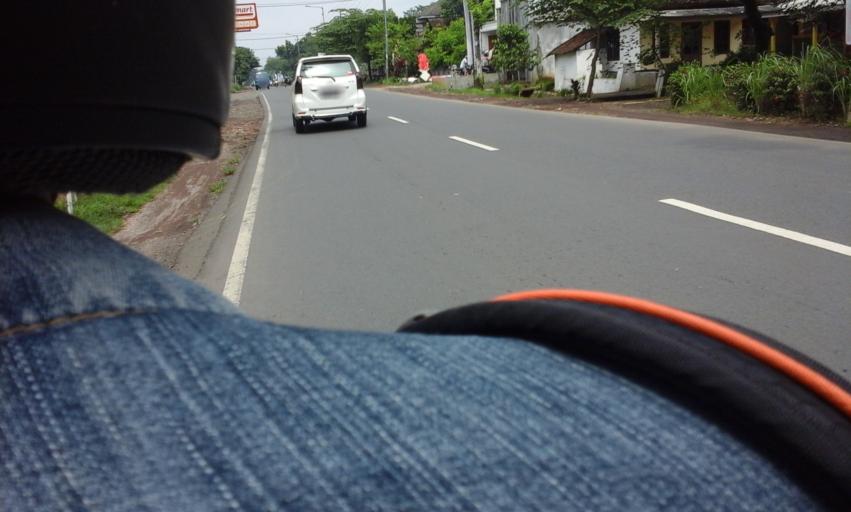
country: ID
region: East Java
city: Klatakan
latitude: -8.1898
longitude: 113.4960
